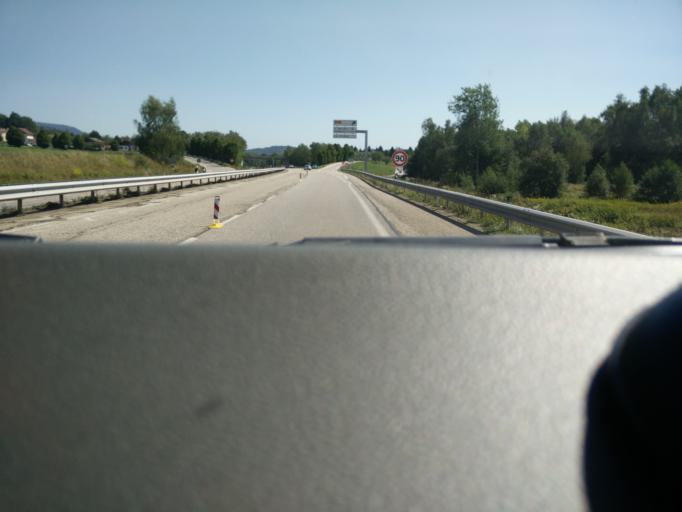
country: FR
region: Lorraine
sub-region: Departement des Vosges
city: Saint-Michel-sur-Meurthe
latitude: 48.3311
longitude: 6.8978
